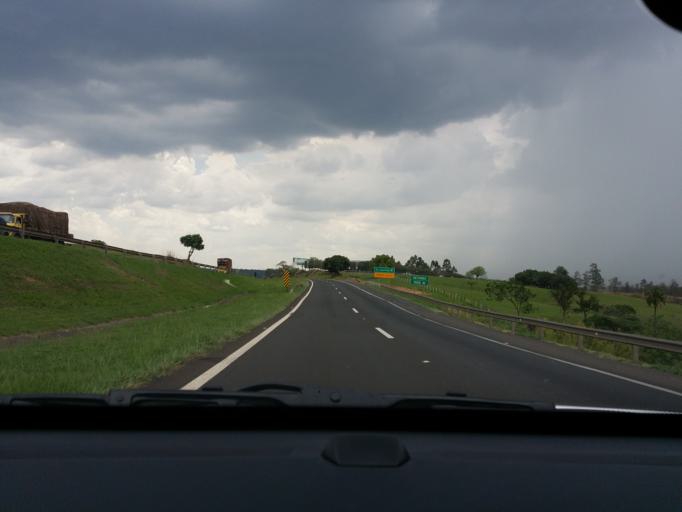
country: BR
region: Sao Paulo
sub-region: Rio Claro
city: Rio Claro
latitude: -22.3407
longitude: -47.6512
